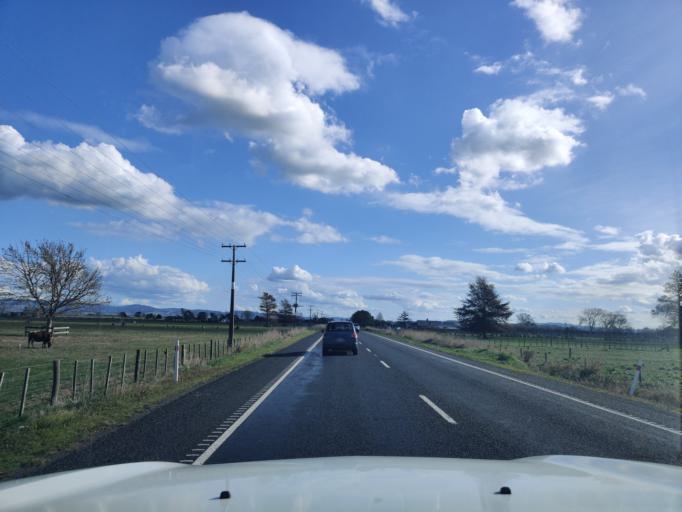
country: NZ
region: Waikato
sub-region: Hauraki District
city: Ngatea
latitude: -37.2726
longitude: 175.5200
